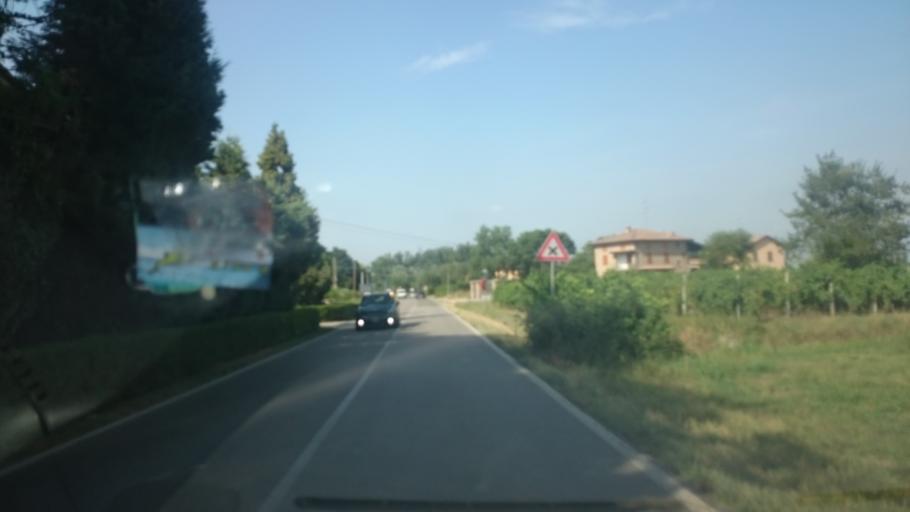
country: IT
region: Emilia-Romagna
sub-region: Provincia di Reggio Emilia
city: Arceto
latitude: 44.6375
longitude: 10.7348
